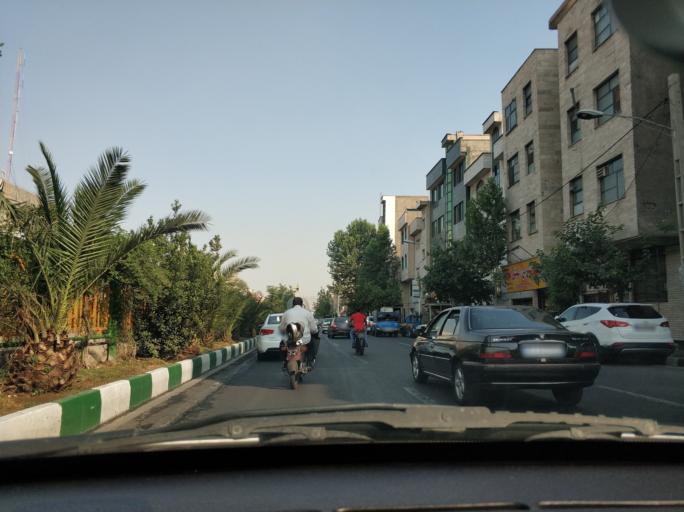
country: IR
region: Tehran
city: Tehran
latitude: 35.7286
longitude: 51.4667
